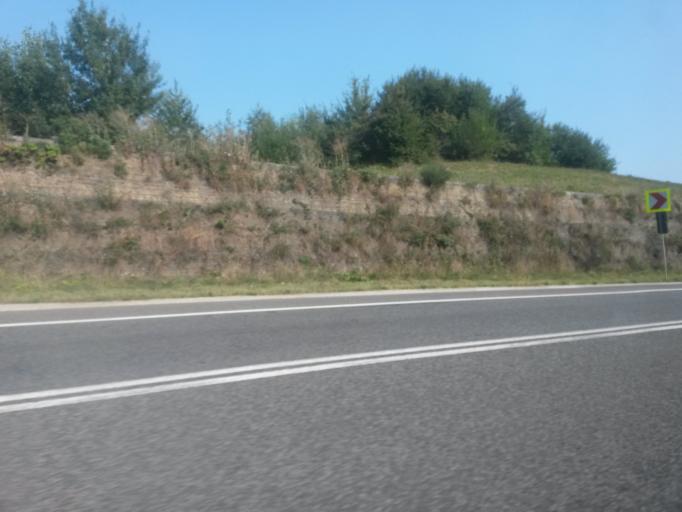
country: RO
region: Cluj
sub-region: Comuna Feleacu
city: Gheorghieni
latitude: 46.7158
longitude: 23.6626
